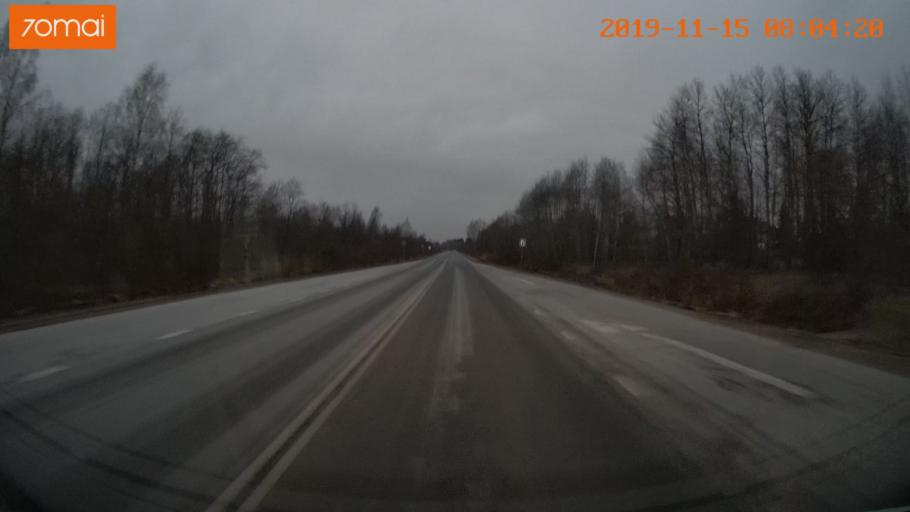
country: RU
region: Vologda
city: Cherepovets
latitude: 59.0073
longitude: 38.0777
